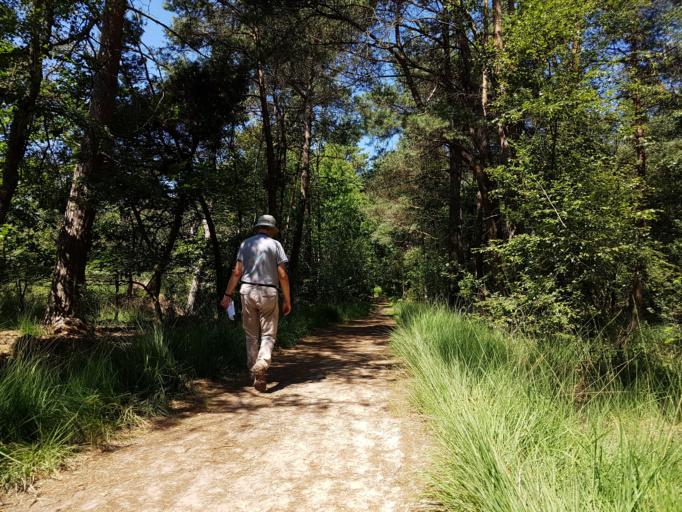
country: NL
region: North Brabant
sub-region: Gemeente Haaren
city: Haaren
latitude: 51.5715
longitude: 5.2391
